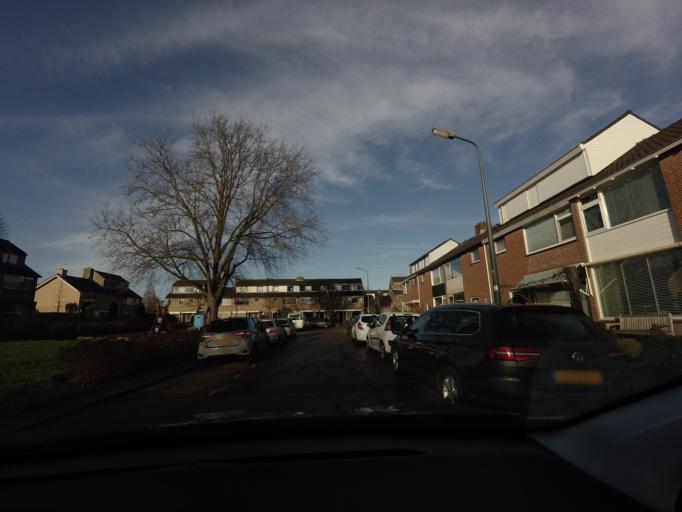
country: NL
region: Utrecht
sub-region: Gemeente Woerden
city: Woerden
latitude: 52.0910
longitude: 4.8679
